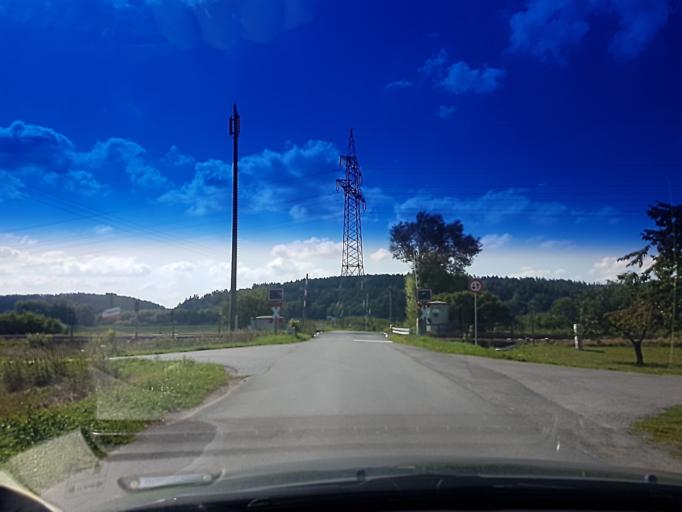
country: DE
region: Bavaria
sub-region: Upper Franconia
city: Mainleus
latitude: 50.1146
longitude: 11.3379
